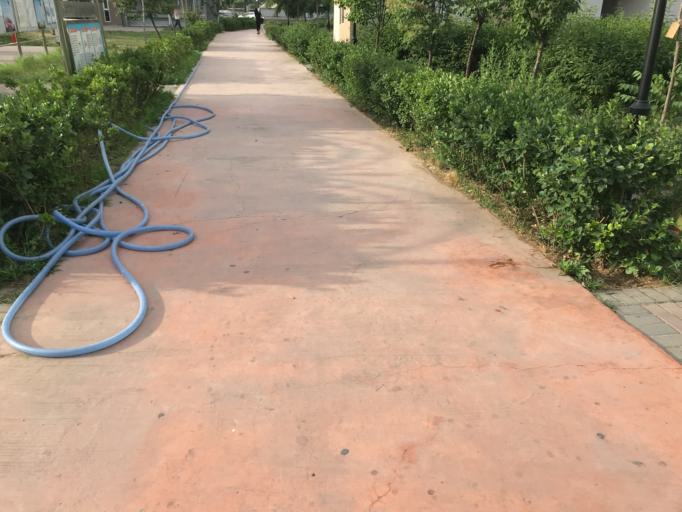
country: CN
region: Beijing
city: Shahe
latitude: 40.1231
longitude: 116.2086
